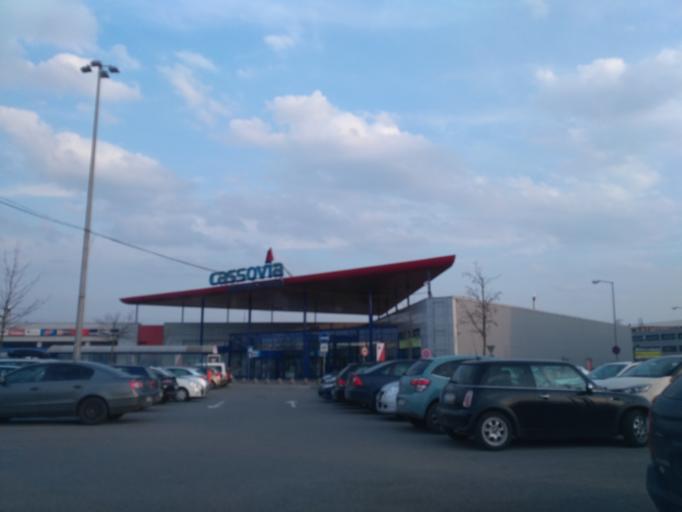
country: SK
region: Kosicky
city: Kosice
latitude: 48.6966
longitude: 21.2495
